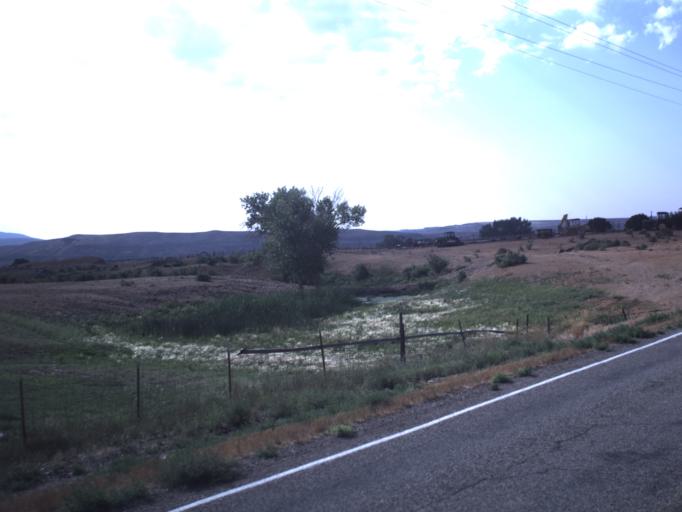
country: US
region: Utah
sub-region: Uintah County
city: Naples
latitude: 40.3935
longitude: -109.3460
